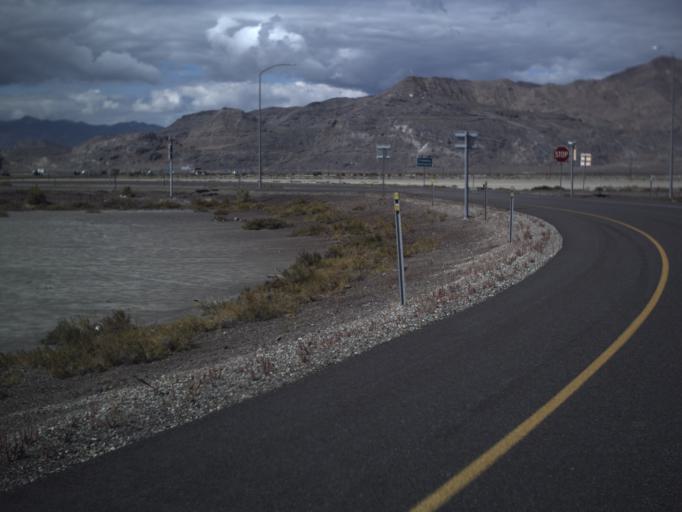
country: US
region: Utah
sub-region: Tooele County
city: Wendover
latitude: 40.7440
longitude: -113.9690
